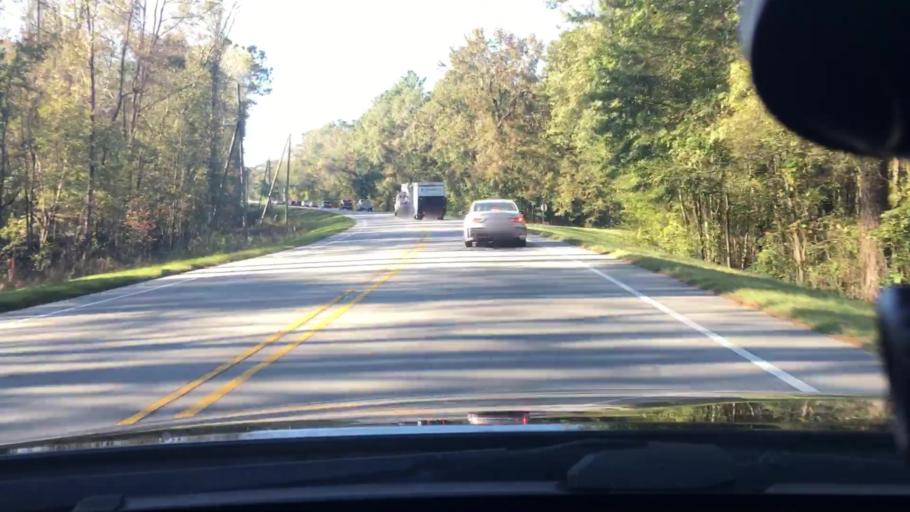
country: US
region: North Carolina
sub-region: Craven County
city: Vanceboro
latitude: 35.2352
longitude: -77.0733
